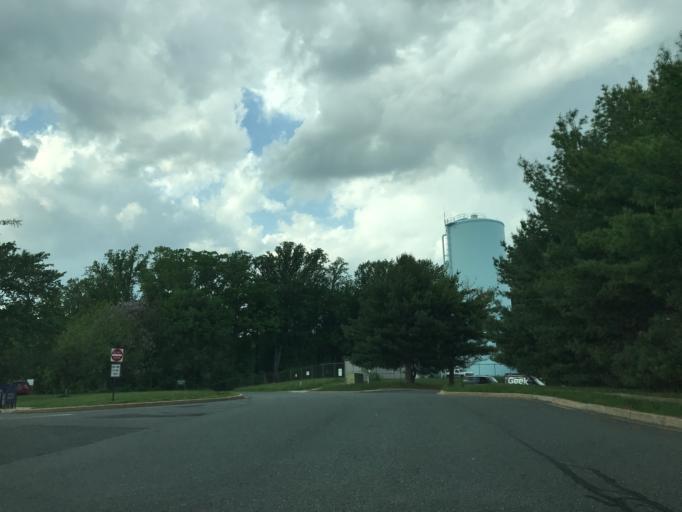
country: US
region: Maryland
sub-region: Harford County
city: North Bel Air
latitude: 39.5282
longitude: -76.3605
